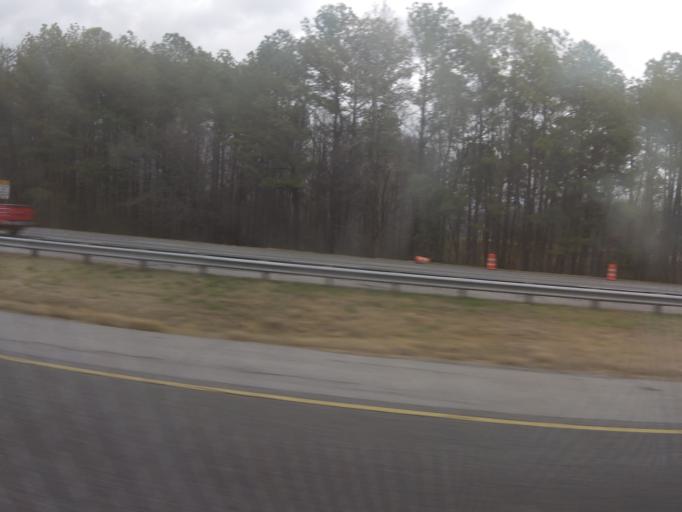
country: US
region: Georgia
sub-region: Whitfield County
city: Dalton
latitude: 34.6358
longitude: -84.9772
